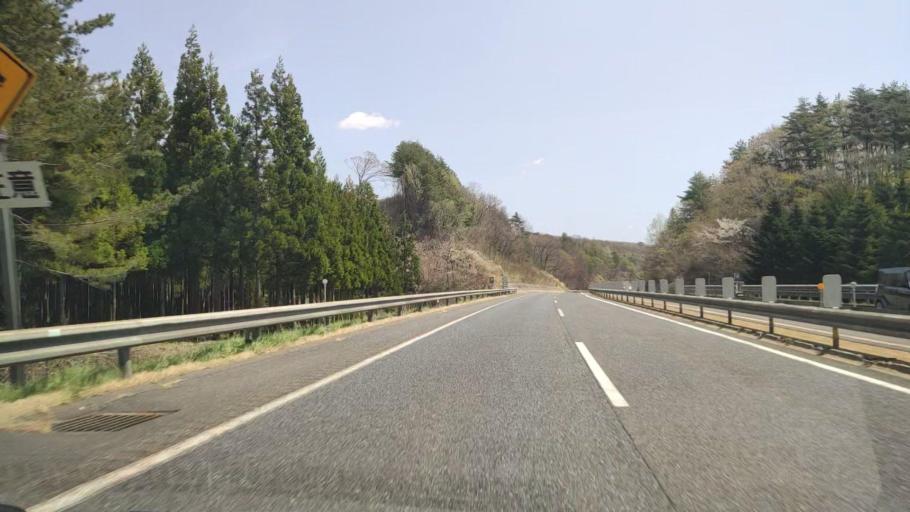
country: JP
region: Iwate
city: Ichinohe
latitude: 40.2161
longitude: 141.2260
